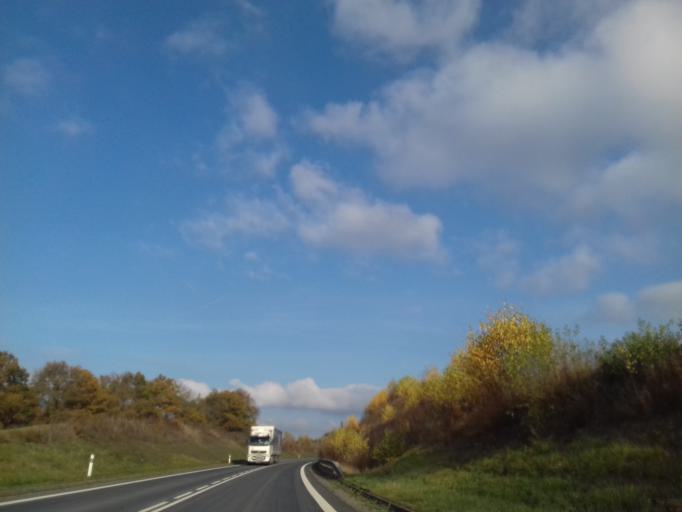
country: CZ
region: Plzensky
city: Horsovsky Tyn
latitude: 49.5165
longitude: 12.9139
